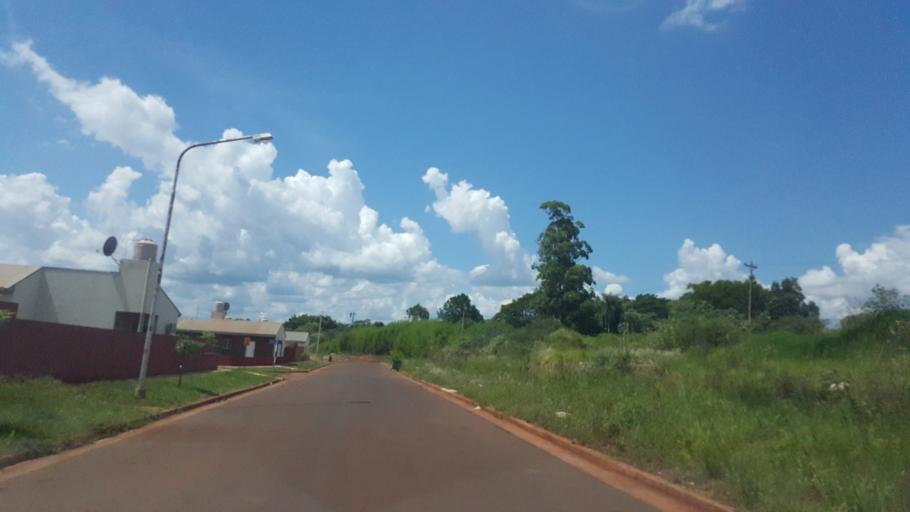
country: AR
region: Misiones
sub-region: Departamento de Capital
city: Posadas
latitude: -27.4083
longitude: -55.9783
